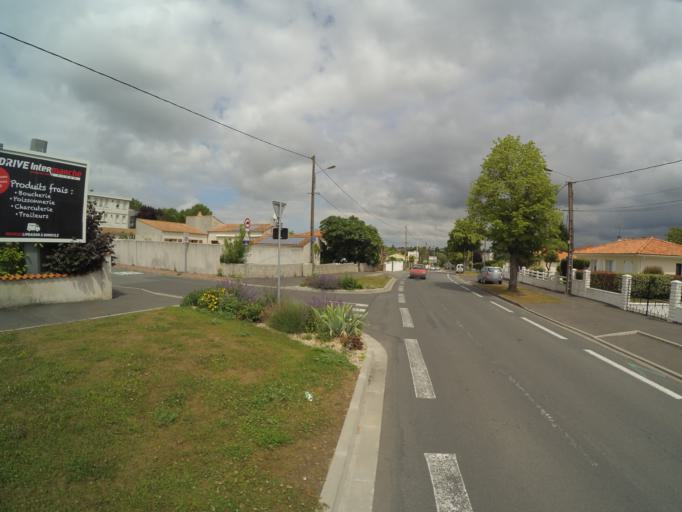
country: FR
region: Poitou-Charentes
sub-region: Departement de la Charente-Maritime
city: Rochefort
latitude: 45.9520
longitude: -0.9685
